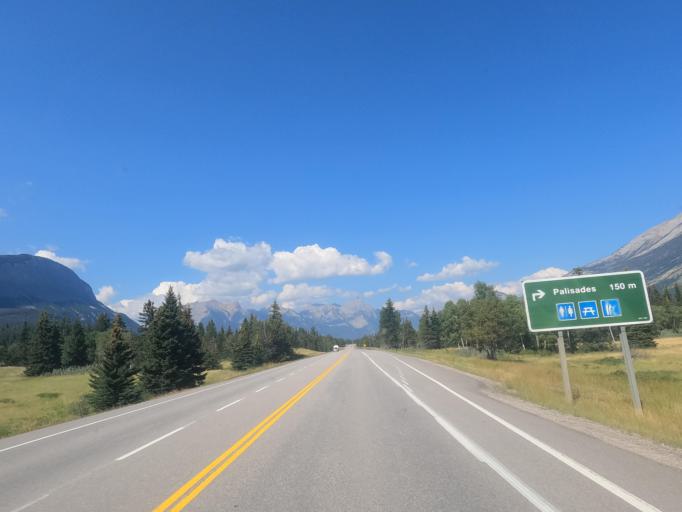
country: CA
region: Alberta
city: Jasper Park Lodge
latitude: 52.9612
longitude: -118.0498
